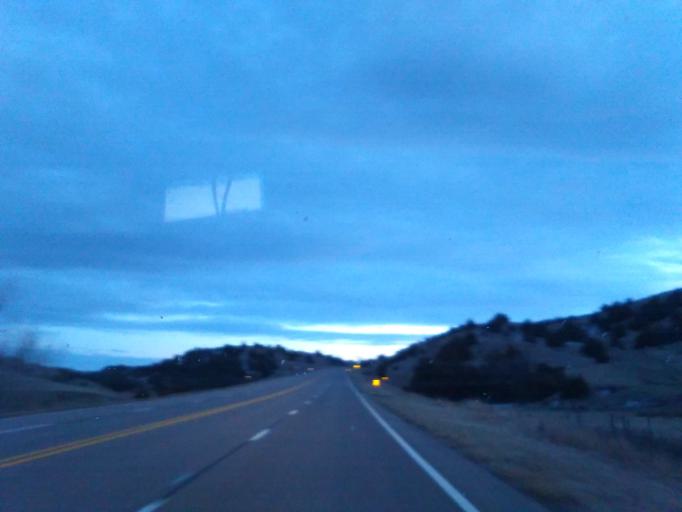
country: US
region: Nebraska
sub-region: Garden County
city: Oshkosh
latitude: 41.2648
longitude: -102.1103
